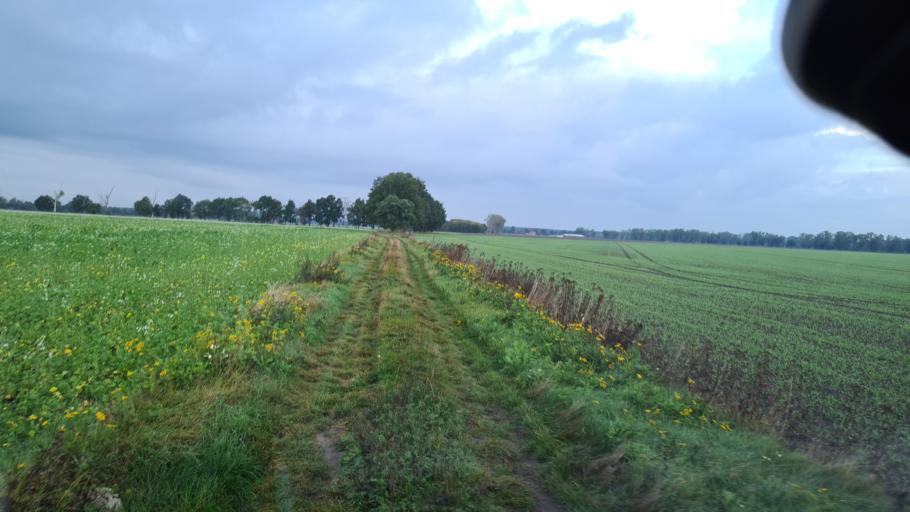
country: DE
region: Brandenburg
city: Schonewalde
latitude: 51.6788
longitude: 13.5705
